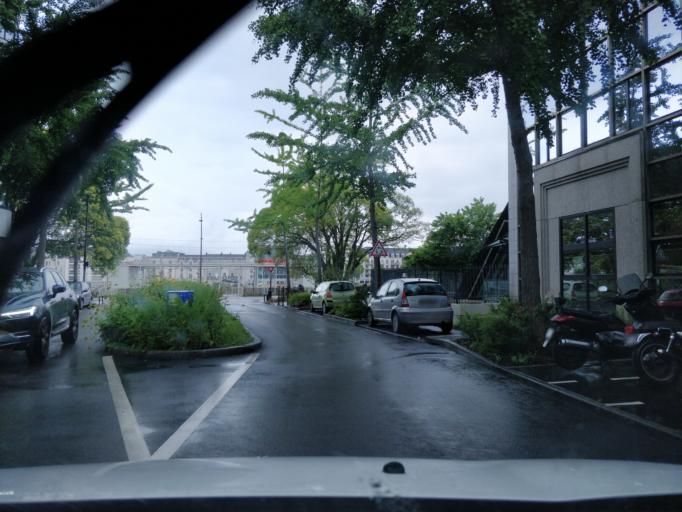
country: FR
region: Pays de la Loire
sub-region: Departement de la Loire-Atlantique
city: Nantes
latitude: 47.2070
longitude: -1.5465
